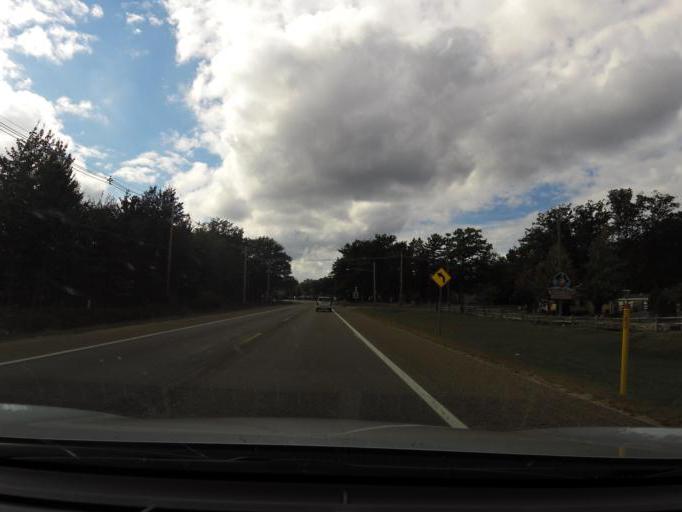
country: US
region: Michigan
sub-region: Roscommon County
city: Prudenville
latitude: 44.3057
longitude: -84.6354
